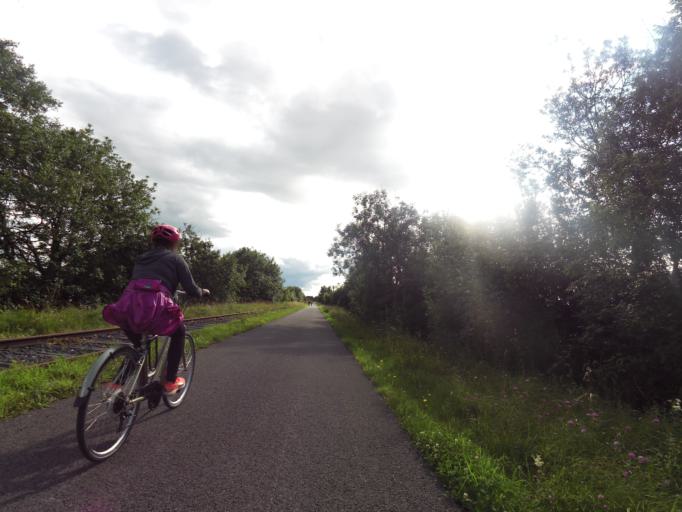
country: IE
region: Leinster
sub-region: An Iarmhi
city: Kilbeggan
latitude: 53.4733
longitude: -7.4873
